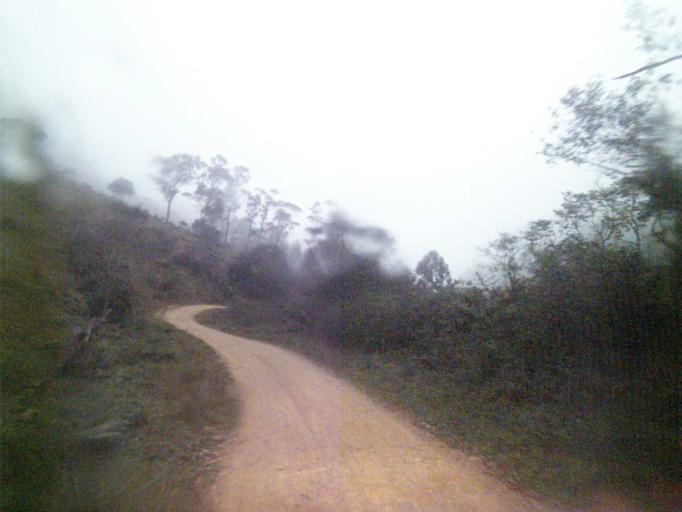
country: BR
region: Santa Catarina
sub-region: Anitapolis
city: Anitapolis
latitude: -27.7947
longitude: -49.1384
